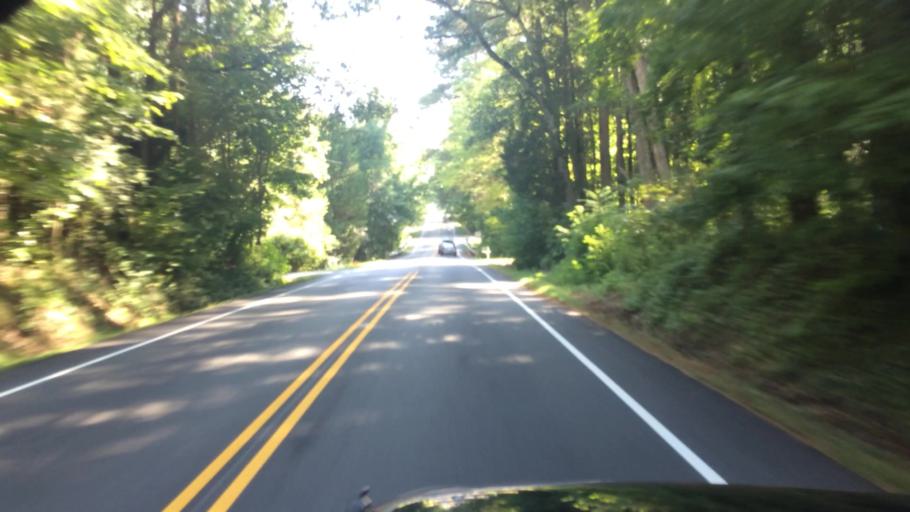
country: US
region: Virginia
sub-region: James City County
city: Williamsburg
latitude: 37.2465
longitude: -76.7391
